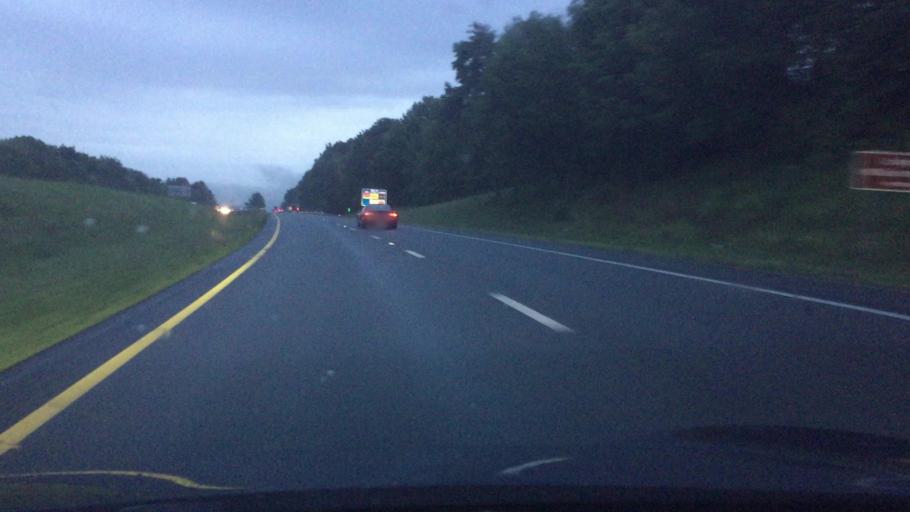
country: US
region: Virginia
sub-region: Wythe County
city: Wytheville
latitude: 36.9658
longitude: -81.0807
